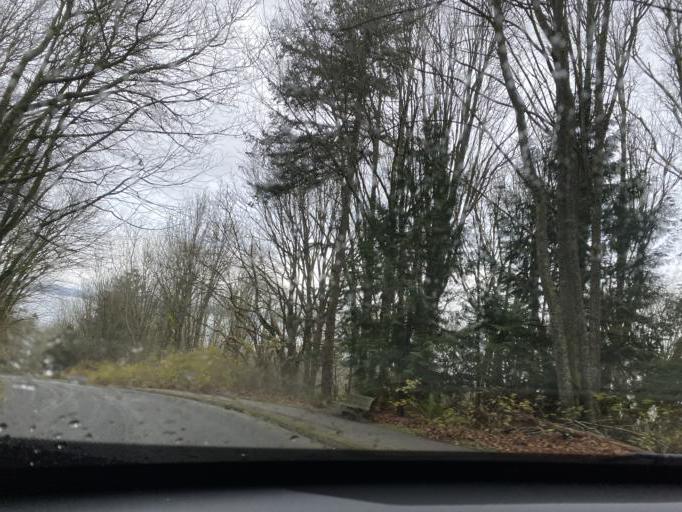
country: US
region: Washington
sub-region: Kitsap County
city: Bainbridge Island
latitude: 47.6616
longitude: -122.4245
